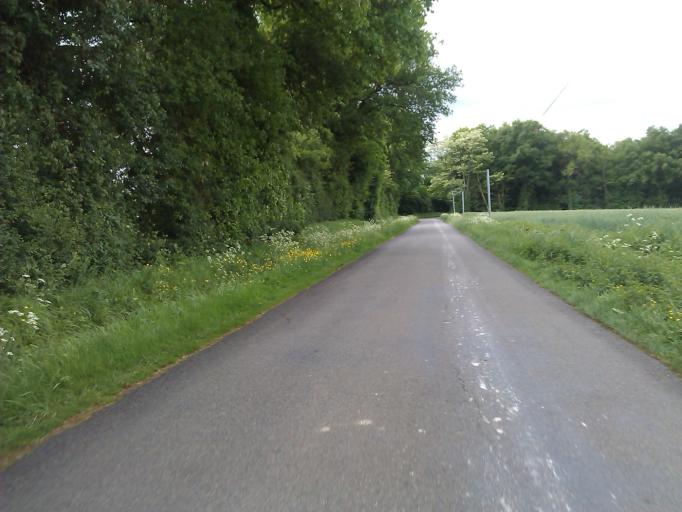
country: FR
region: Poitou-Charentes
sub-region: Departement de la Vienne
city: Charroux
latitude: 46.0993
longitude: 0.5185
